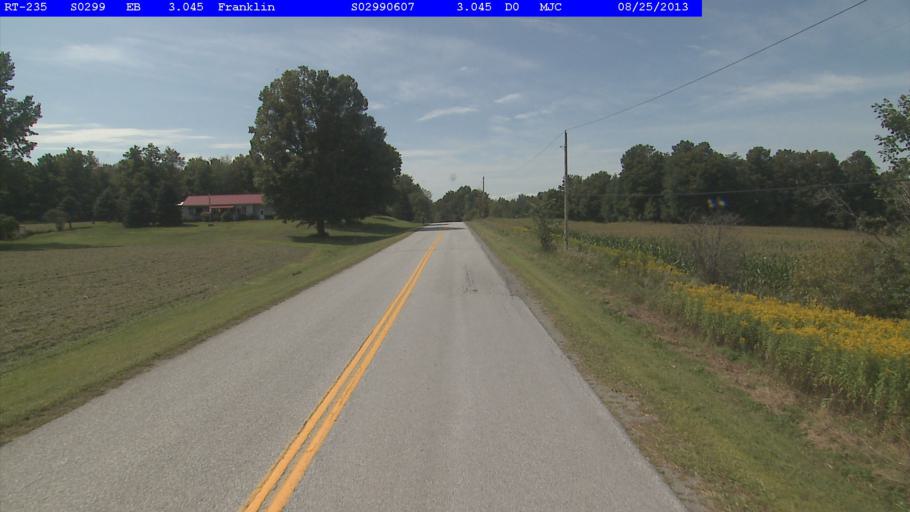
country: CA
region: Quebec
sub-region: Monteregie
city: Bedford
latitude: 45.0027
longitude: -72.9609
